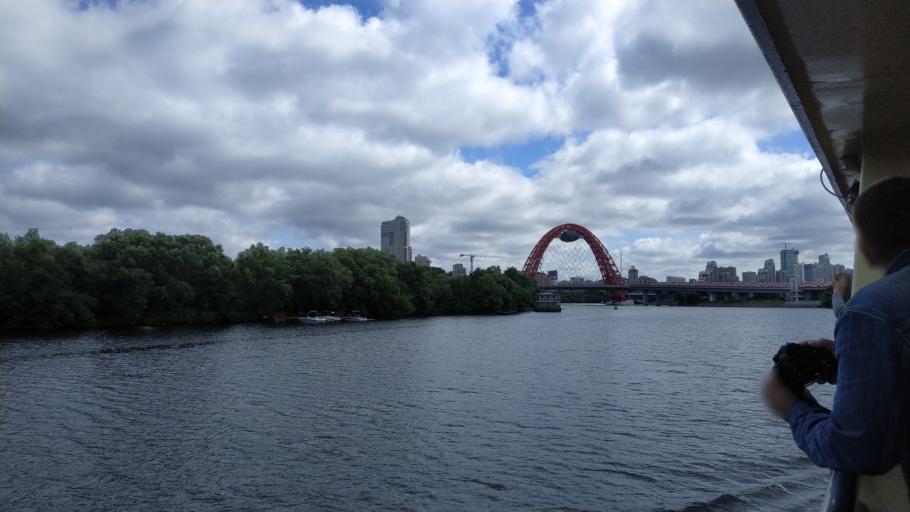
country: RU
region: Moscow
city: Shchukino
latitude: 55.7741
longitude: 37.4299
